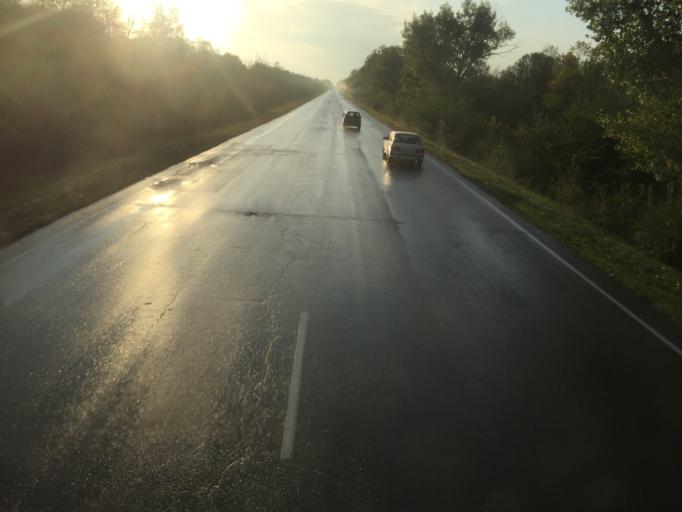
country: RU
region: Rostov
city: Bataysk
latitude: 47.0568
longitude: 39.8246
